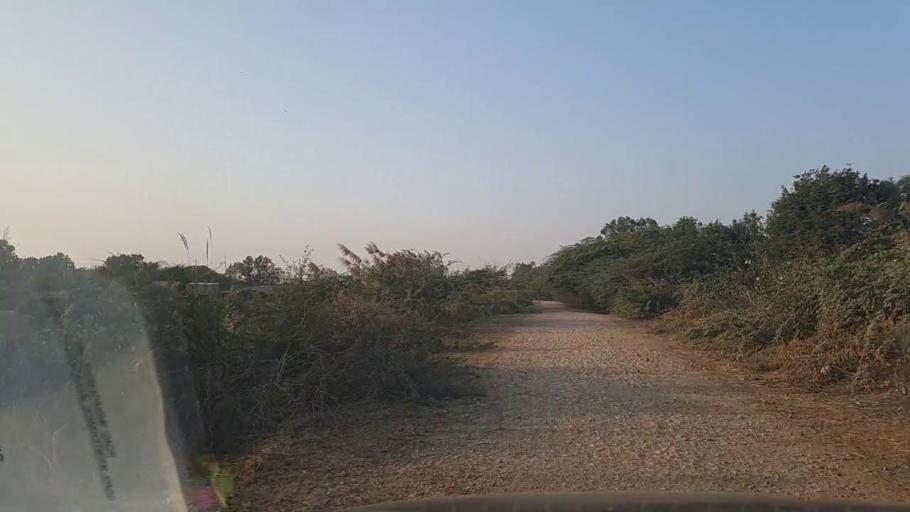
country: PK
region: Sindh
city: Keti Bandar
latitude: 24.3136
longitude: 67.5999
